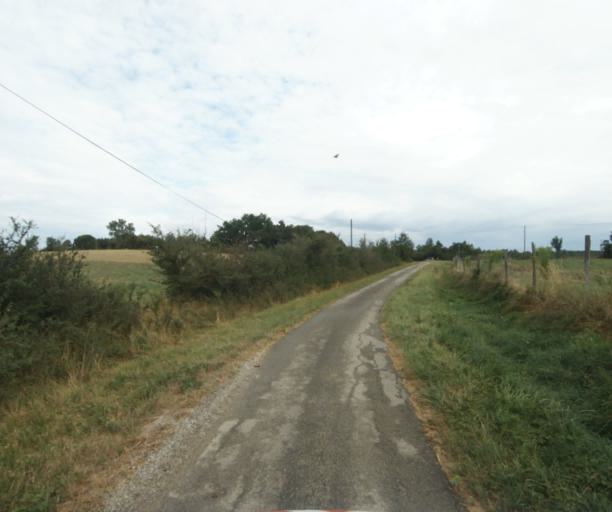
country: FR
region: Midi-Pyrenees
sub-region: Departement de la Haute-Garonne
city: Revel
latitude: 43.4259
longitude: 1.9974
